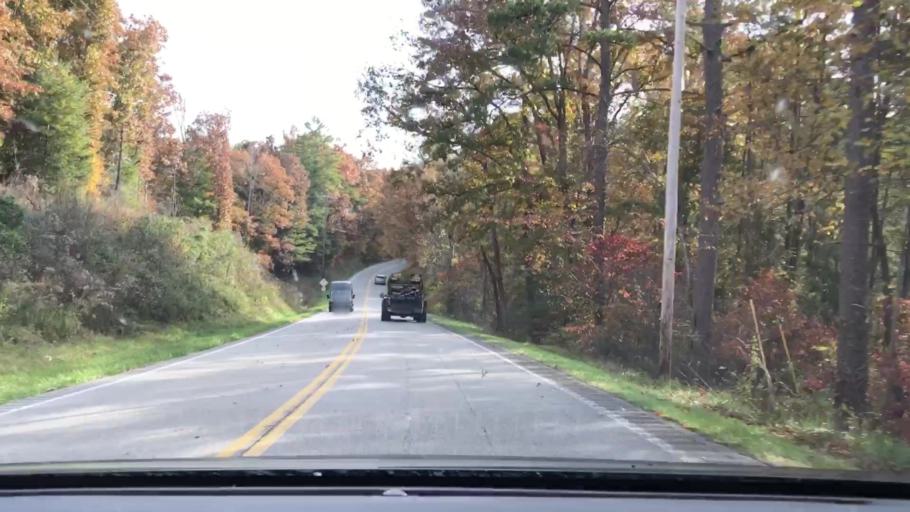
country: US
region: Tennessee
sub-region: Scott County
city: Huntsville
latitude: 36.3498
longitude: -84.6860
